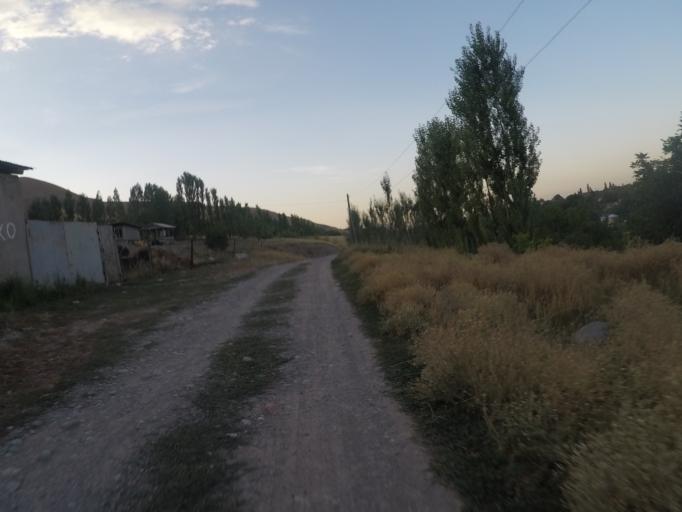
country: KG
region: Chuy
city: Bishkek
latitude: 42.7725
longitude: 74.6399
